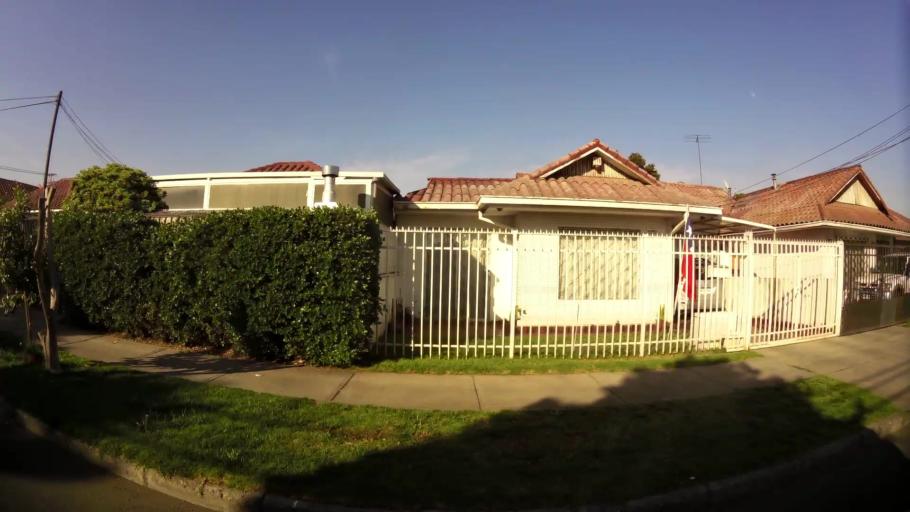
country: CL
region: Santiago Metropolitan
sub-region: Provincia de Santiago
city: Lo Prado
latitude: -33.4847
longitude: -70.7490
